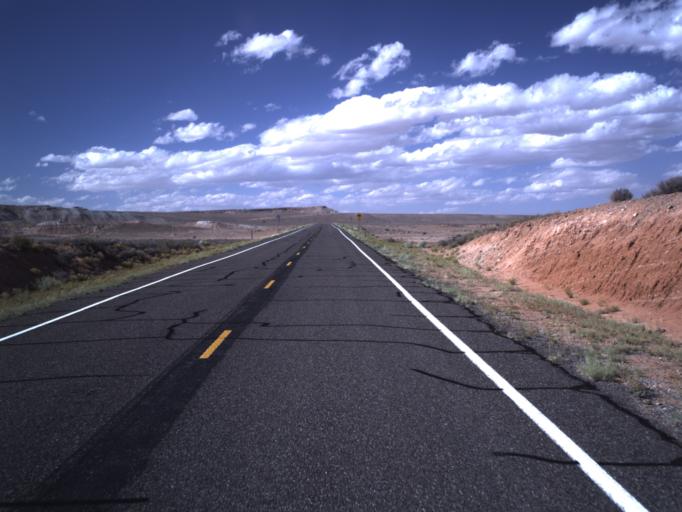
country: US
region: Utah
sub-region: Wayne County
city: Loa
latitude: 38.0937
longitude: -110.6197
